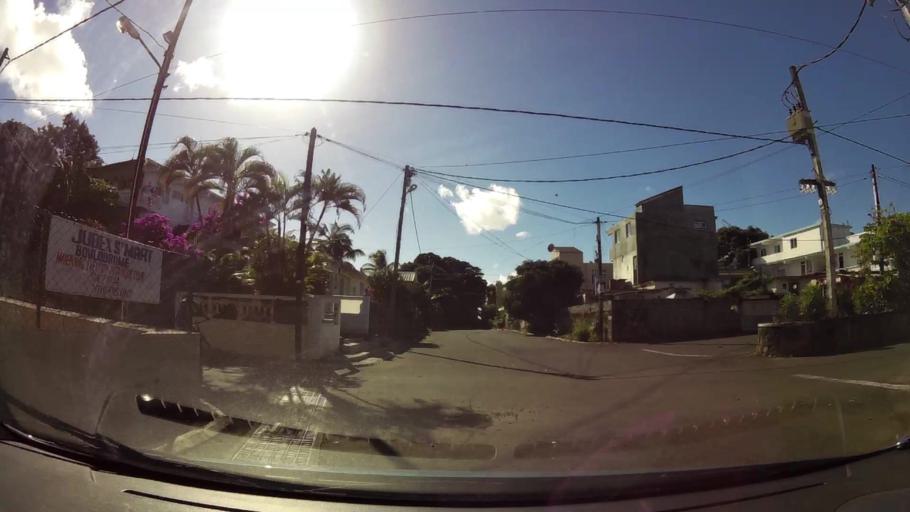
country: MU
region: Grand Port
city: Mahebourg
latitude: -20.4099
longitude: 57.7106
